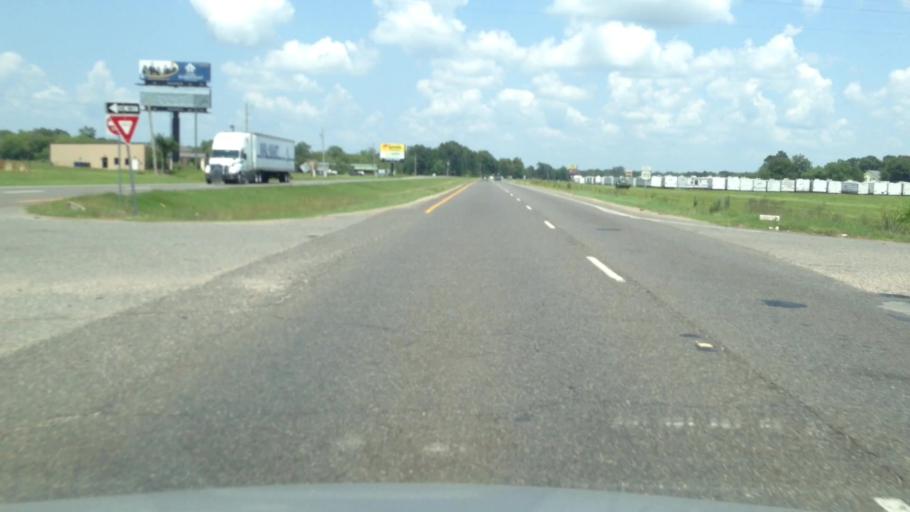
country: US
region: Louisiana
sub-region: Saint Landry Parish
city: Port Barre
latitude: 30.5460
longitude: -92.0100
